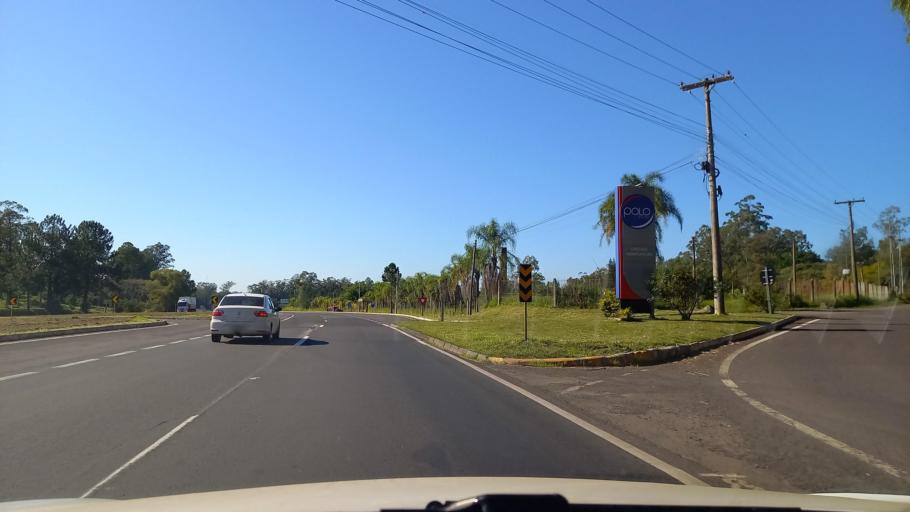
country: BR
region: Rio Grande do Sul
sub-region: Montenegro
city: Montenegro
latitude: -29.8172
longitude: -51.3930
